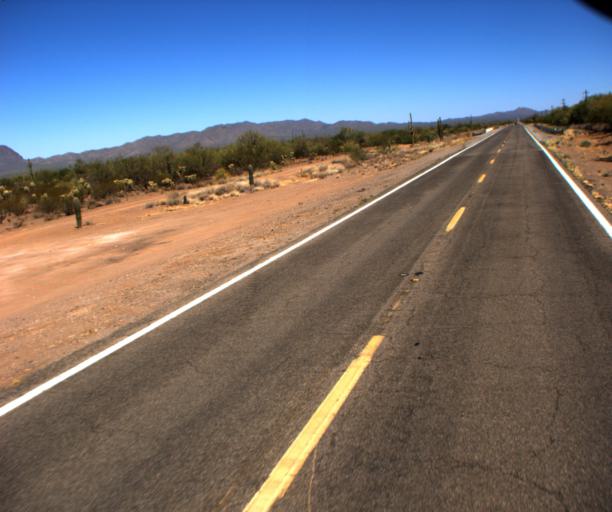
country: US
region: Arizona
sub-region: Pima County
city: Sells
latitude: 32.0577
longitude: -112.0315
